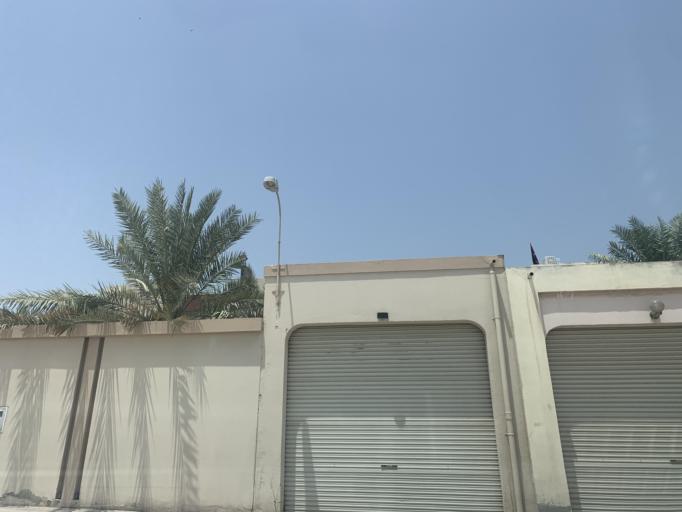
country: BH
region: Central Governorate
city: Madinat Hamad
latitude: 26.1464
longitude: 50.5027
